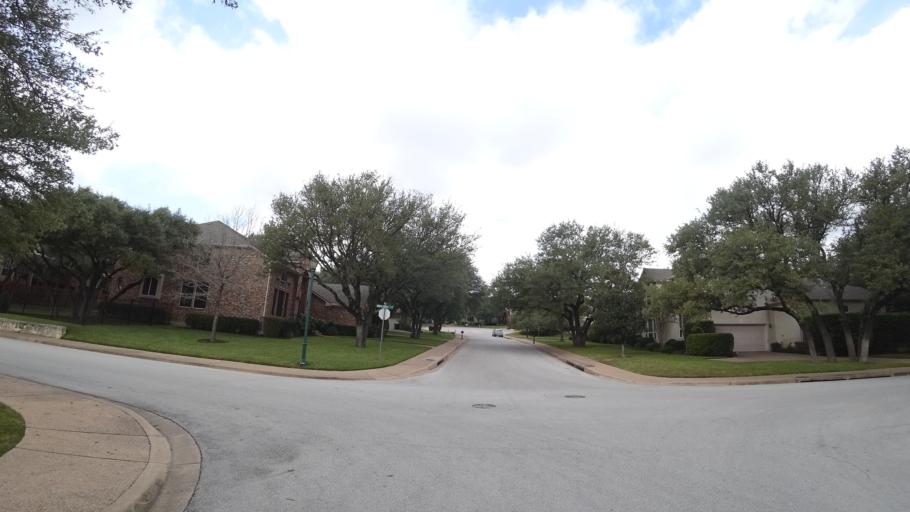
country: US
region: Texas
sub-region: Travis County
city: Barton Creek
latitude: 30.3101
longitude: -97.8985
